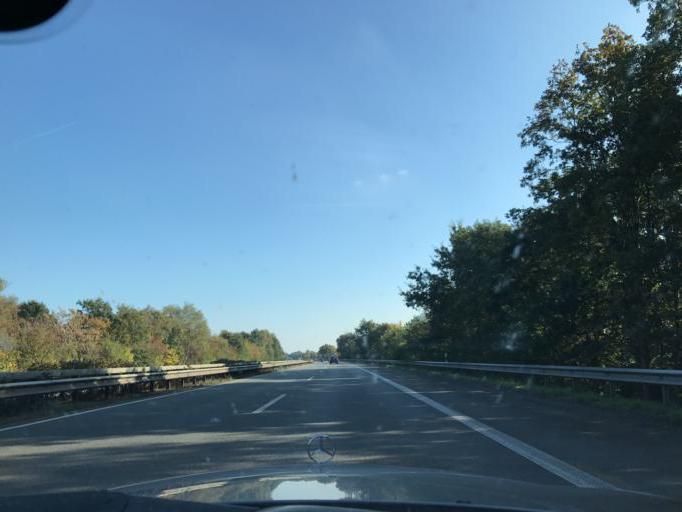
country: DE
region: Lower Saxony
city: Hatten
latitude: 53.0715
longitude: 8.3289
